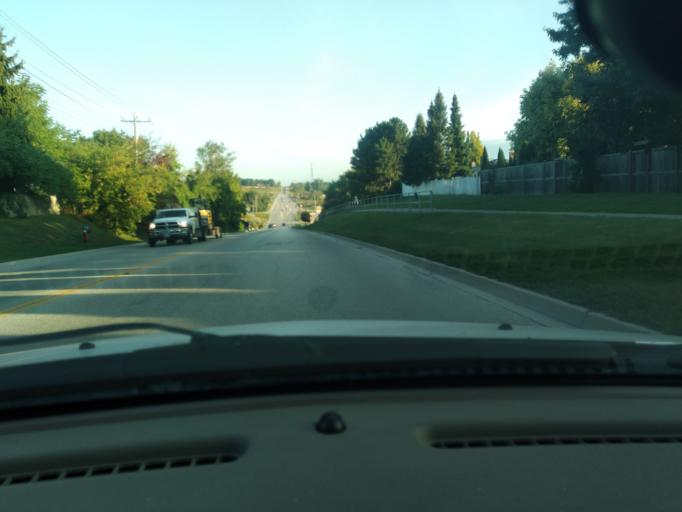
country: CA
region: Ontario
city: Bradford West Gwillimbury
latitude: 44.1225
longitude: -79.5668
